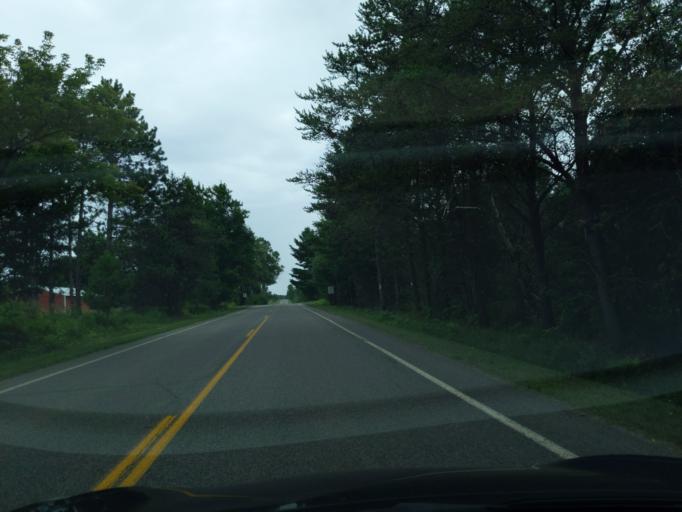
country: US
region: Michigan
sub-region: Clare County
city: Harrison
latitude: 44.0276
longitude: -84.9494
